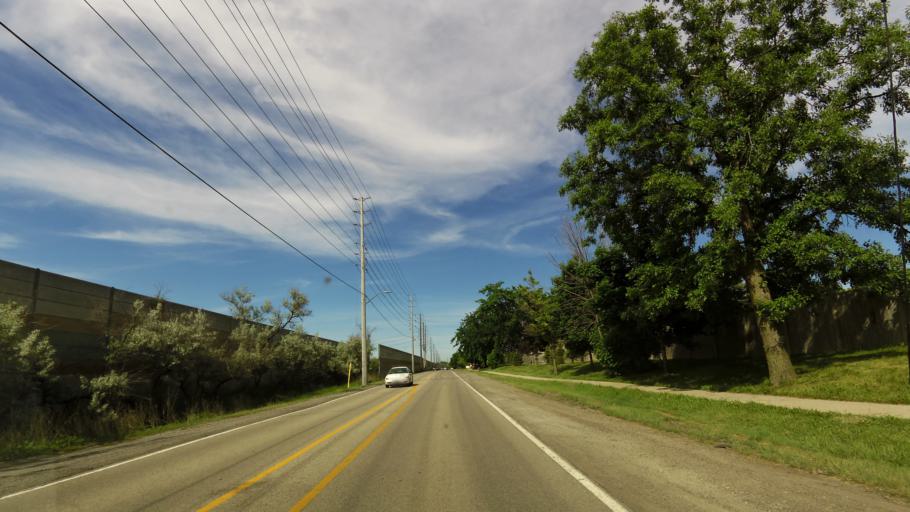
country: CA
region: Ontario
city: Mississauga
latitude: 43.5413
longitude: -79.6288
